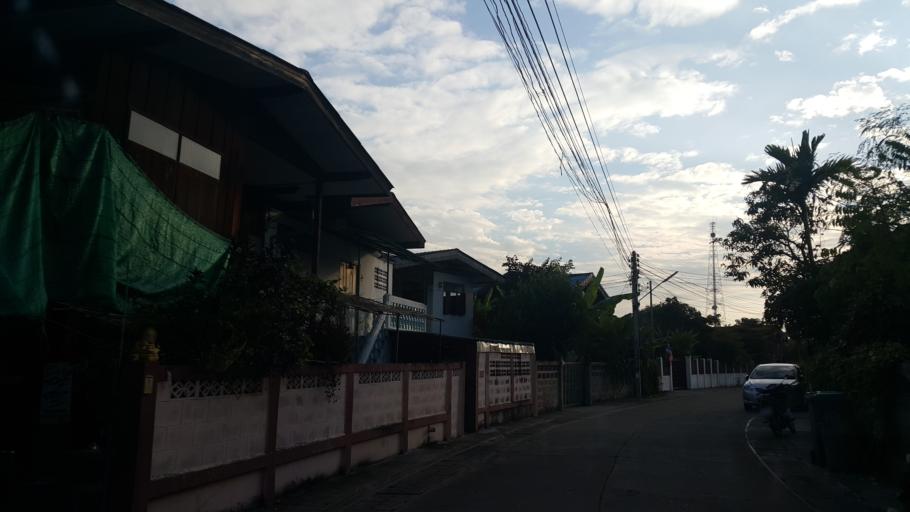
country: TH
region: Lampang
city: Sop Prap
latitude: 17.8826
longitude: 99.3354
